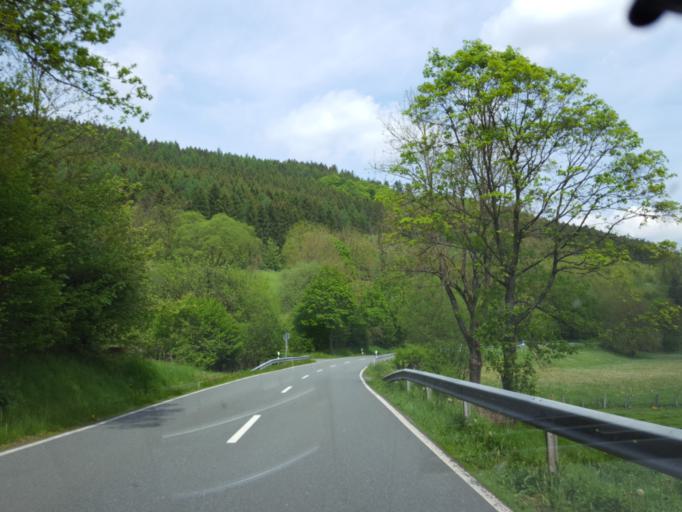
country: DE
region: North Rhine-Westphalia
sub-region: Regierungsbezirk Arnsberg
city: Olsberg
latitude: 51.2853
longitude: 8.4805
